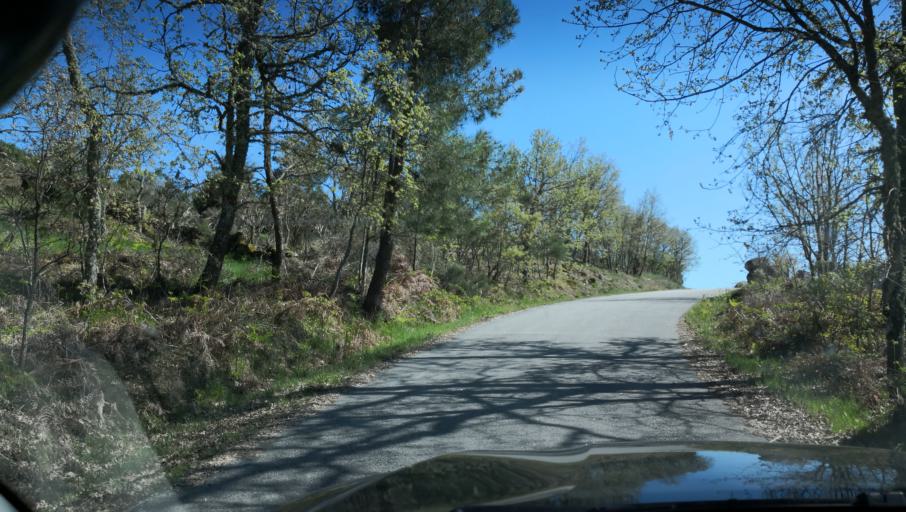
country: PT
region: Vila Real
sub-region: Sabrosa
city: Sabrosa
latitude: 41.2959
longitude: -7.6322
